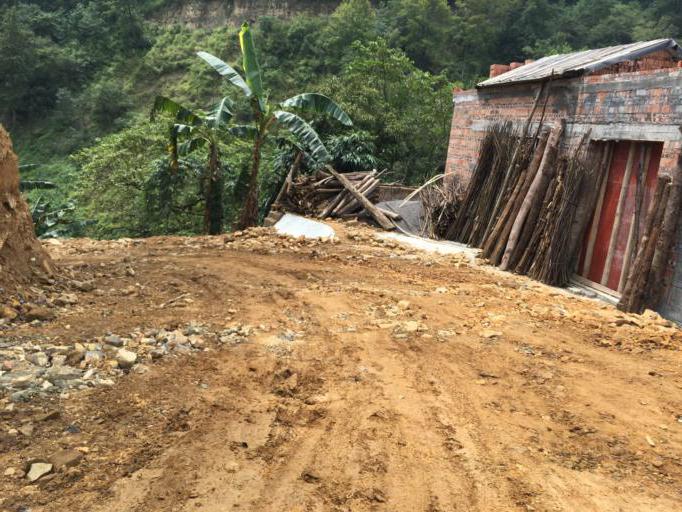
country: CN
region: Guangxi Zhuangzu Zizhiqu
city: Tongle
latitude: 25.2994
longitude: 106.1409
